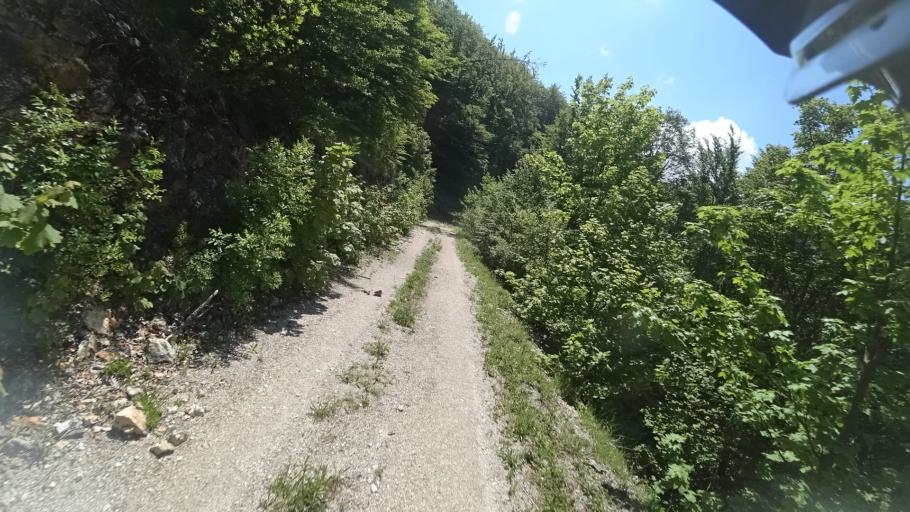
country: BA
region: Federation of Bosnia and Herzegovina
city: Orasac
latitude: 44.5680
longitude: 15.8532
